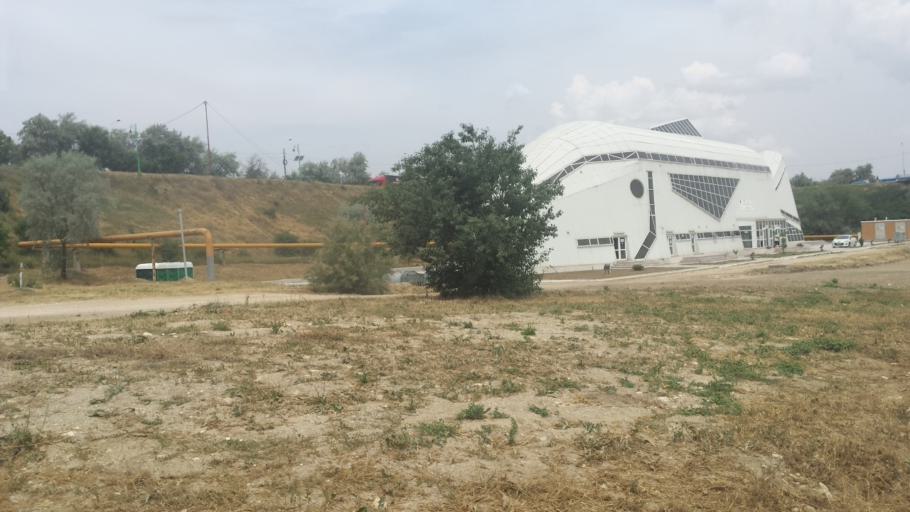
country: RO
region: Constanta
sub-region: Comuna Navodari
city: Navodari
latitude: 44.3207
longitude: 28.6187
